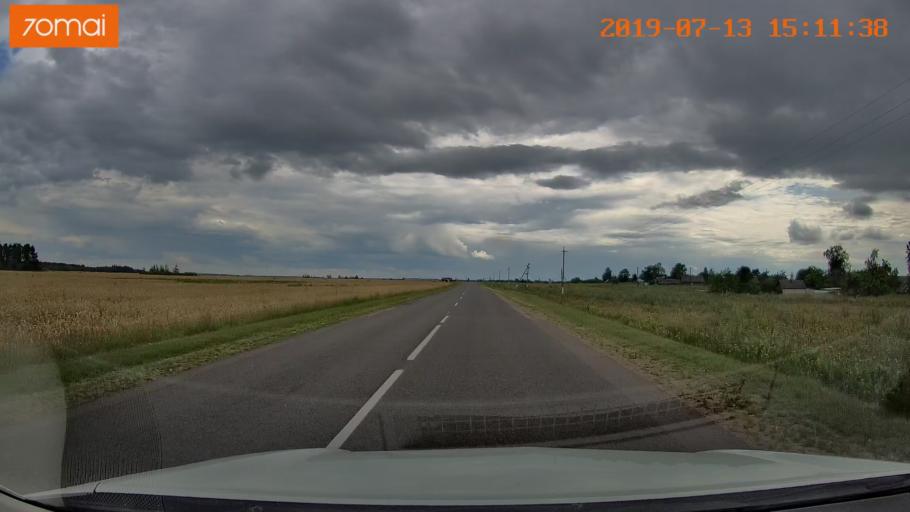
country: BY
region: Mogilev
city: Hlusha
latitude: 53.1587
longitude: 28.7865
